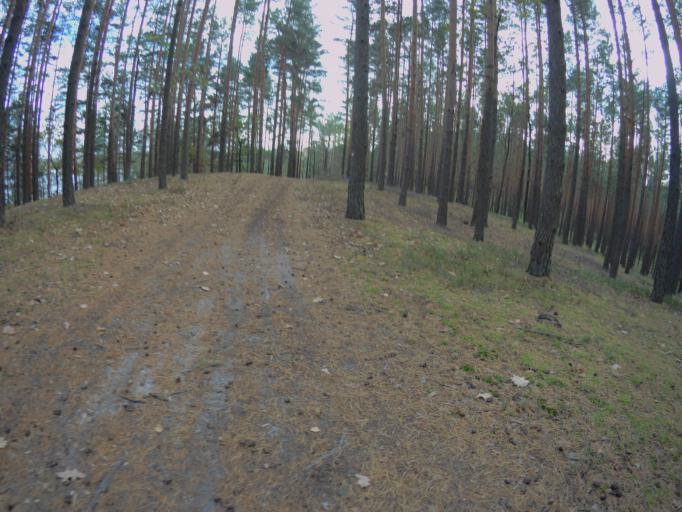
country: PL
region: Subcarpathian Voivodeship
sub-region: Powiat kolbuszowski
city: Lipnica
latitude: 50.3291
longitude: 21.9356
